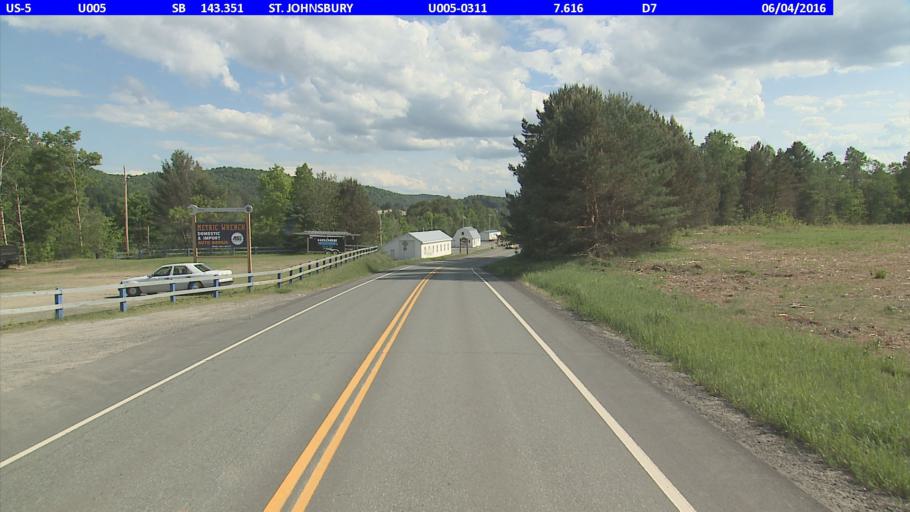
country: US
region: Vermont
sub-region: Caledonia County
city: Lyndon
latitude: 44.4977
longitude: -72.0044
